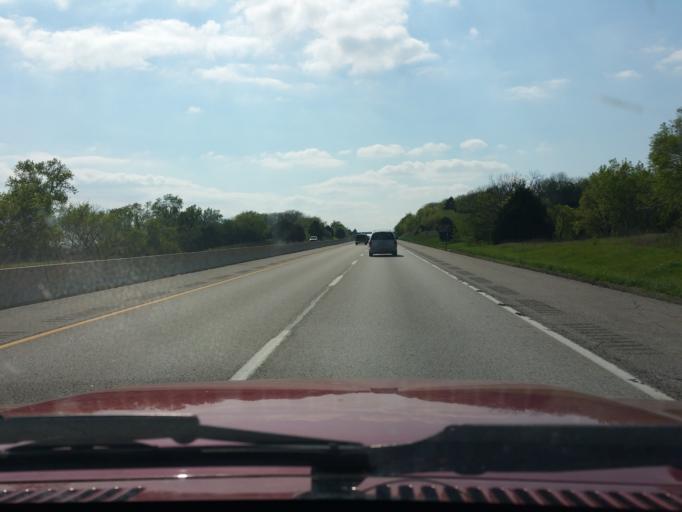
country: US
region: Kansas
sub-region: Douglas County
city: Lawrence
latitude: 38.9979
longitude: -95.3064
